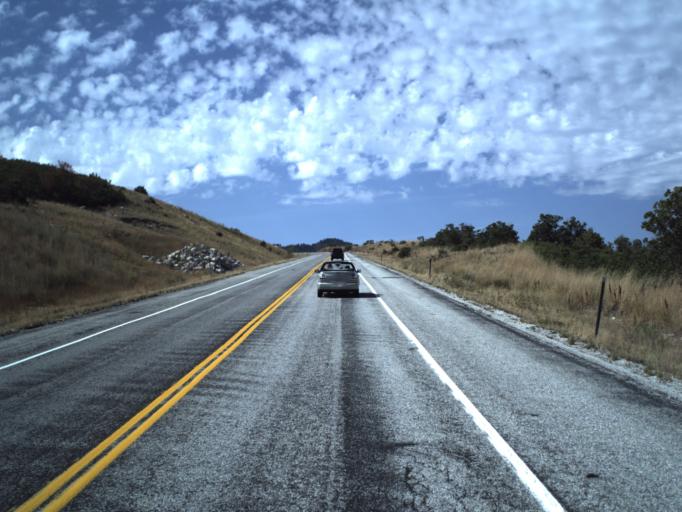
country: US
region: Utah
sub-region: Morgan County
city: Mountain Green
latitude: 41.2094
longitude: -111.8408
